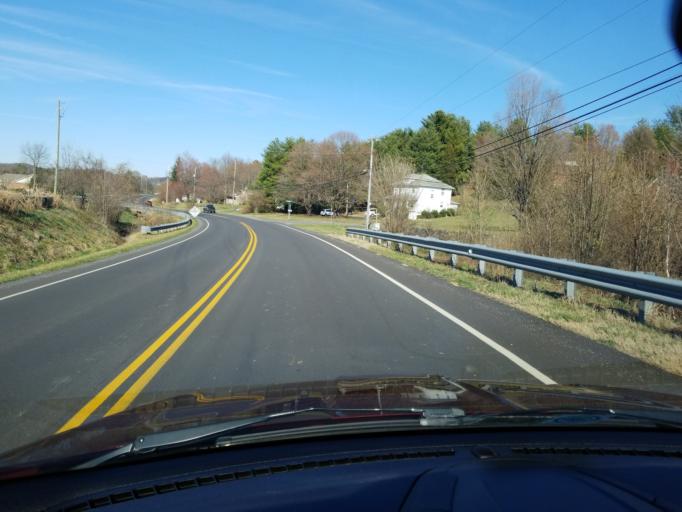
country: US
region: Virginia
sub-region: Botetourt County
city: Cloverdale
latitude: 37.3551
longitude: -79.9137
